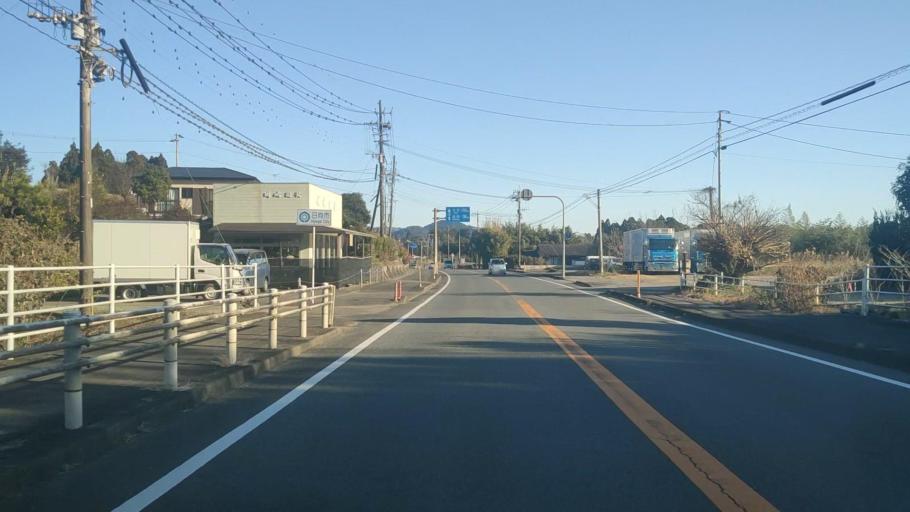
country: JP
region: Miyazaki
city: Takanabe
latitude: 32.3066
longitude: 131.5834
